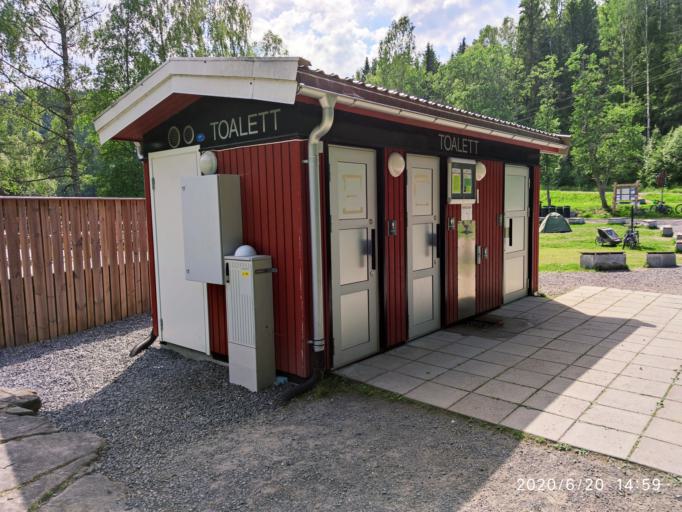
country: NO
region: Akershus
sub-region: Lorenskog
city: Kjenn
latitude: 59.8767
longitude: 10.9894
